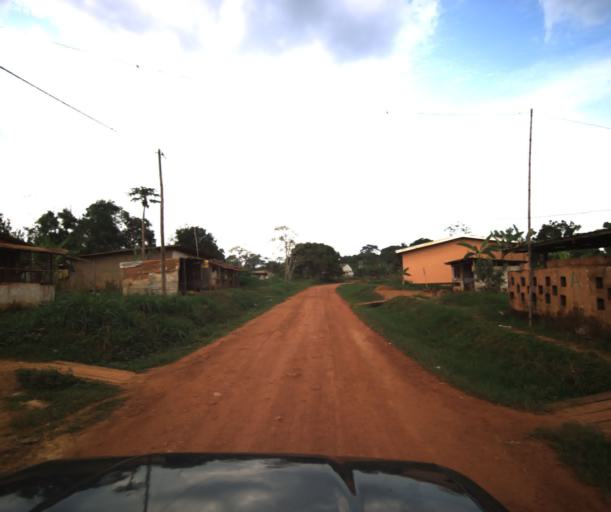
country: CM
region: Centre
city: Akono
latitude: 3.6010
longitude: 11.1816
